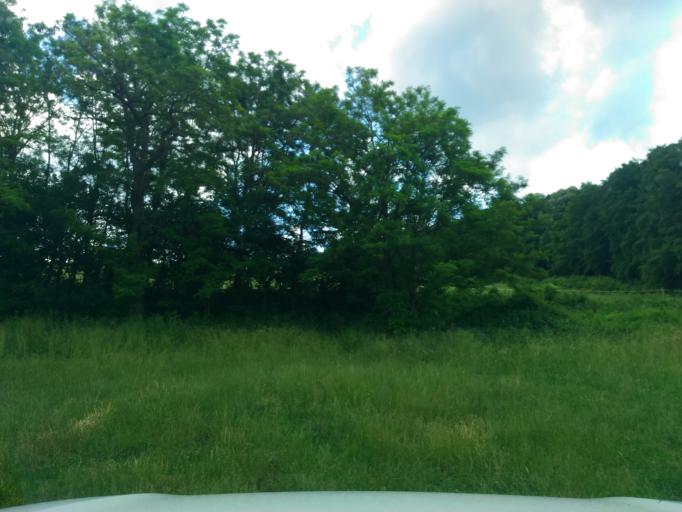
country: HU
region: Baranya
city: Komlo
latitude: 46.1579
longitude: 18.2261
